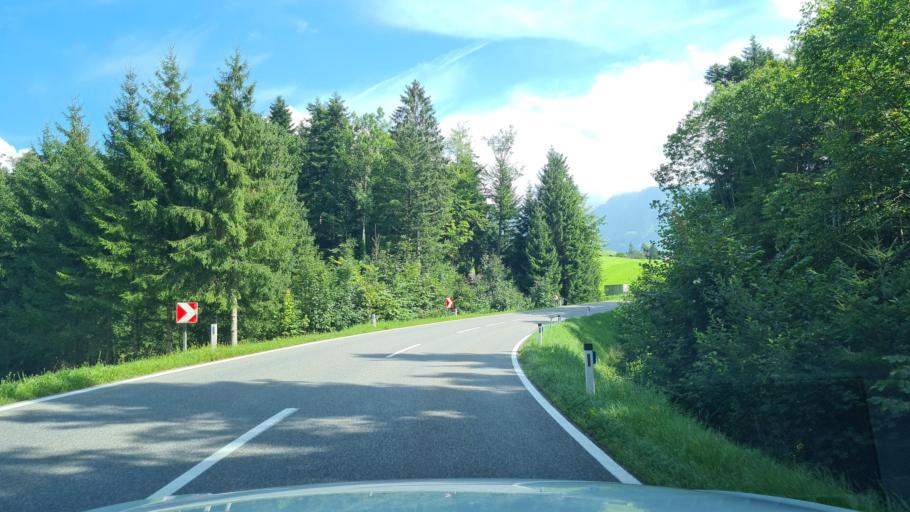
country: AT
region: Vorarlberg
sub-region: Politischer Bezirk Bregenz
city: Egg
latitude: 47.4508
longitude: 9.8962
